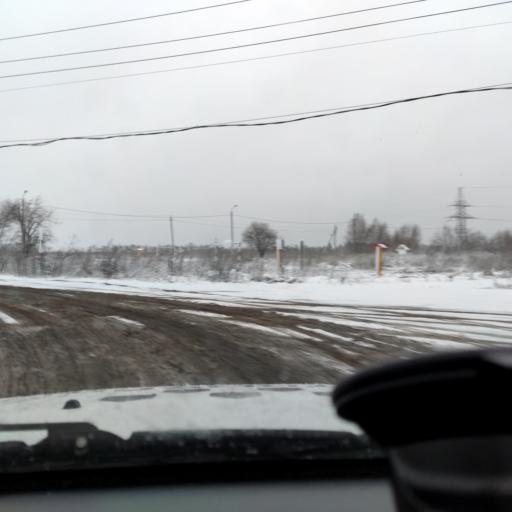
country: RU
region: Perm
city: Perm
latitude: 58.0379
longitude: 56.3881
